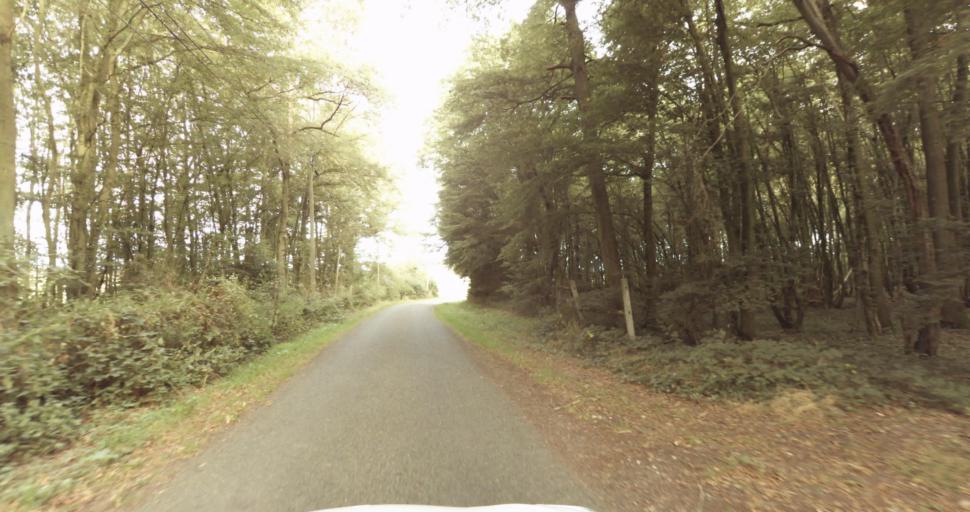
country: FR
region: Haute-Normandie
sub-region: Departement de l'Eure
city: Saint-Germain-sur-Avre
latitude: 48.8301
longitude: 1.2517
